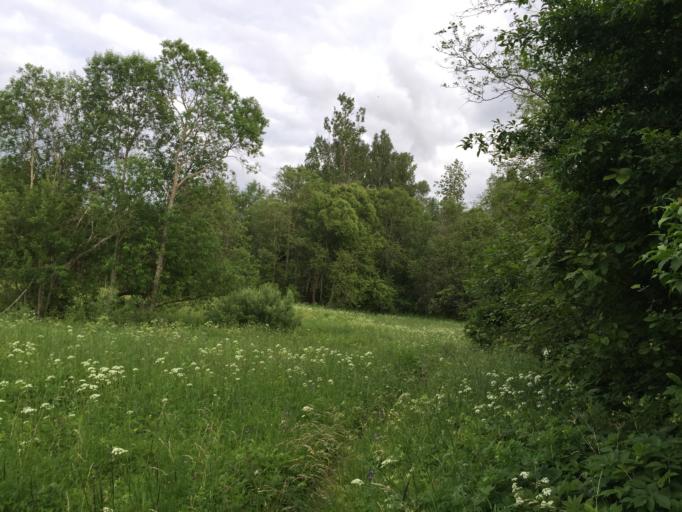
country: LV
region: Ligatne
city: Ligatne
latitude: 57.2425
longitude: 25.1464
